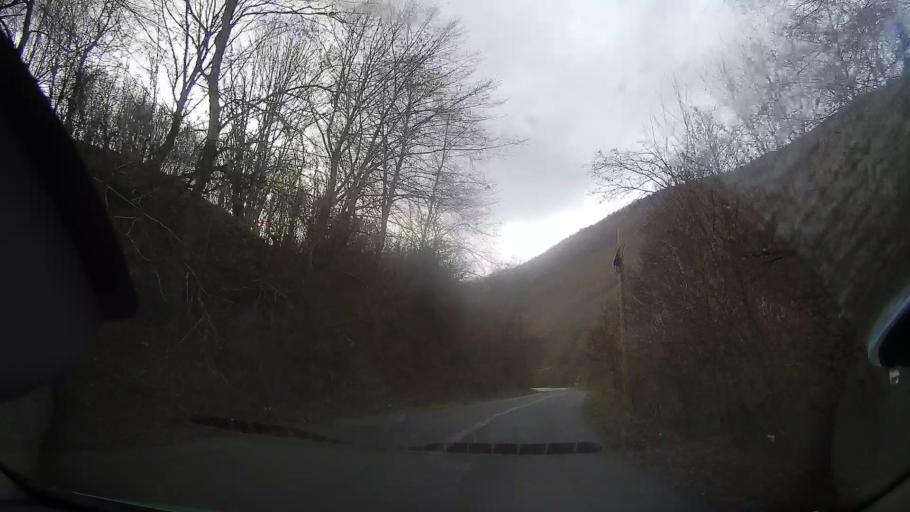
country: RO
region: Alba
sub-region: Comuna Rimetea
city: Rimetea
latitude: 46.4944
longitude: 23.5809
